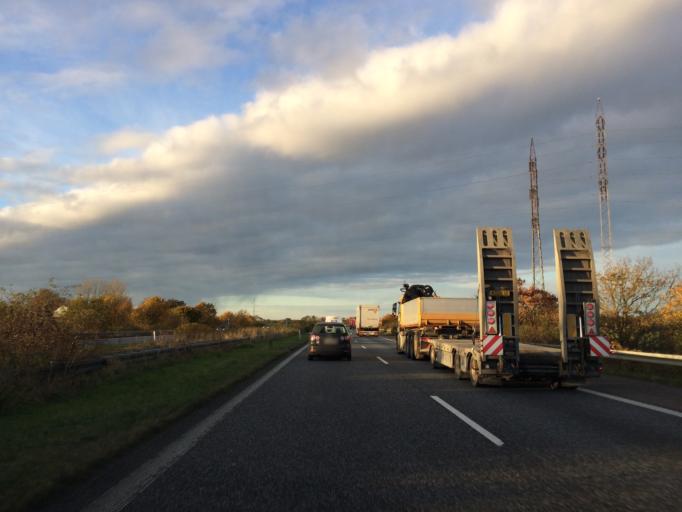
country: DK
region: South Denmark
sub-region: Aabenraa Kommune
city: Rodekro
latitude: 55.0296
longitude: 9.3580
